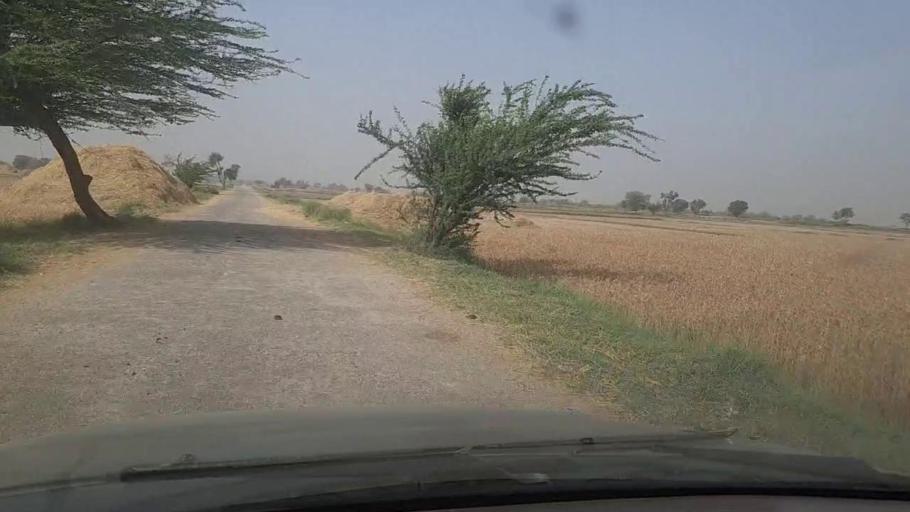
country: PK
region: Sindh
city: Garhi Yasin
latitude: 27.8846
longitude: 68.5731
